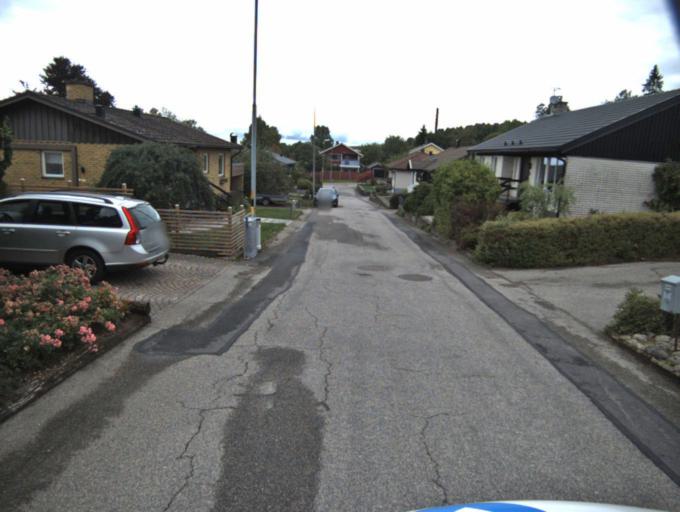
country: SE
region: Vaestra Goetaland
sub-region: Ulricehamns Kommun
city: Ulricehamn
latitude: 57.7871
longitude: 13.4273
